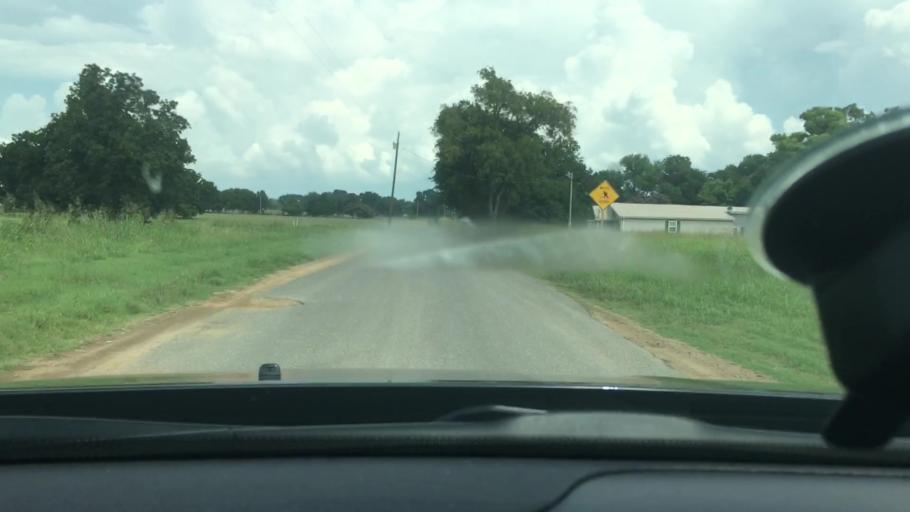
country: US
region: Oklahoma
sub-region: Carter County
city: Dickson
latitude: 34.2017
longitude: -96.8982
